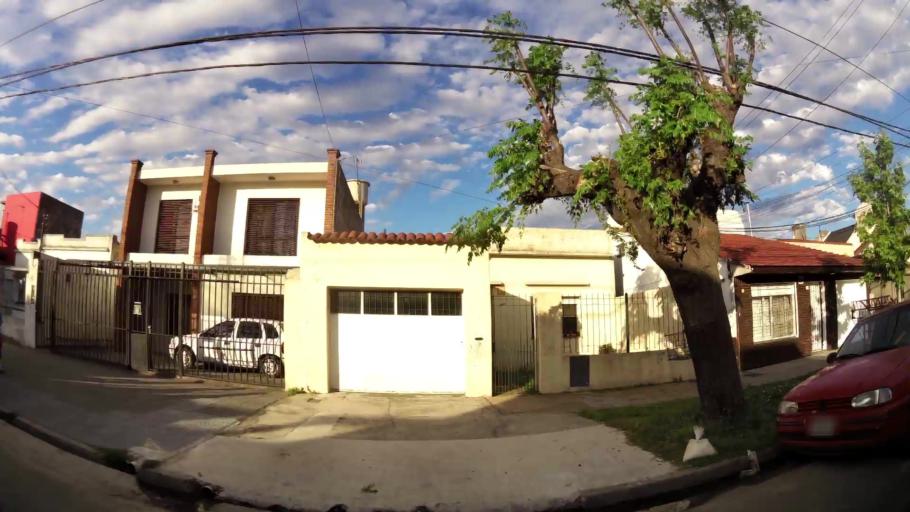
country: AR
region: Buenos Aires
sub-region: Partido de Avellaneda
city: Avellaneda
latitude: -34.6924
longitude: -58.3433
